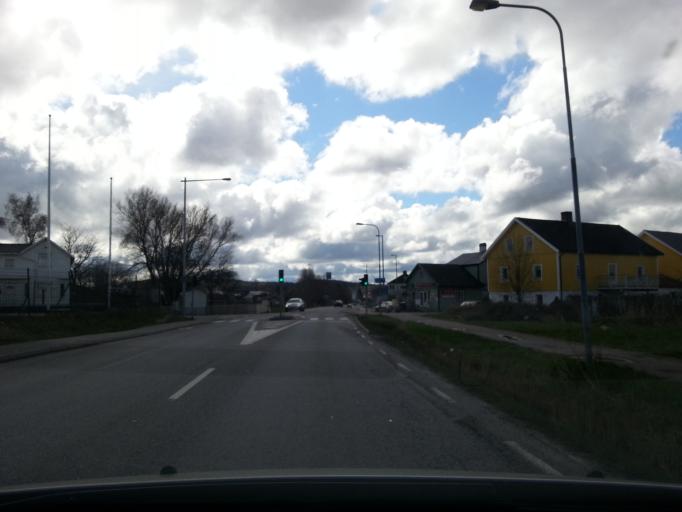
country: SE
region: Vaestra Goetaland
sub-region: Kungalvs Kommun
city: Kungalv
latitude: 57.8022
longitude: 11.9121
